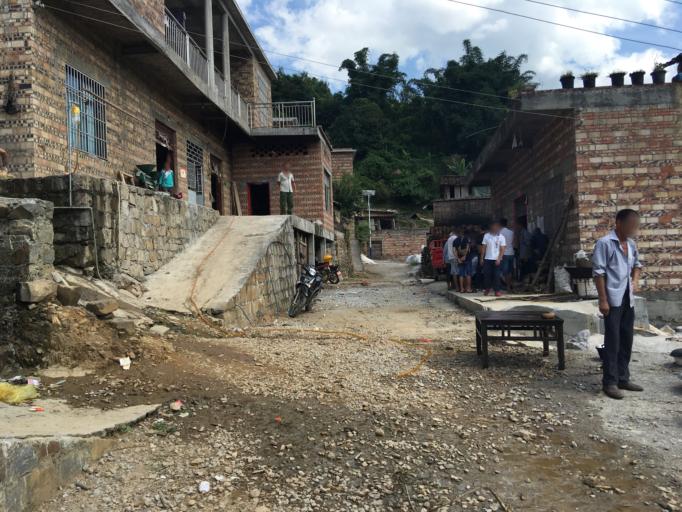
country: CN
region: Guangxi Zhuangzu Zizhiqu
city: Tongle
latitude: 24.9697
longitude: 105.9869
